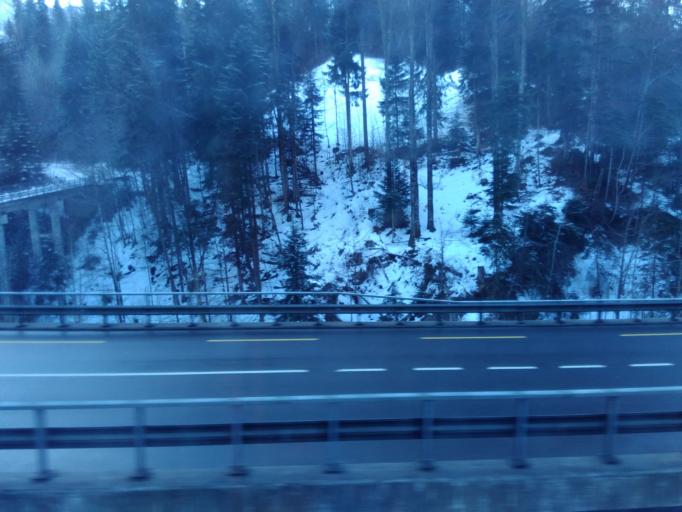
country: CH
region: Schwyz
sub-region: Bezirk Schwyz
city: Sattel
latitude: 47.0870
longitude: 8.6511
